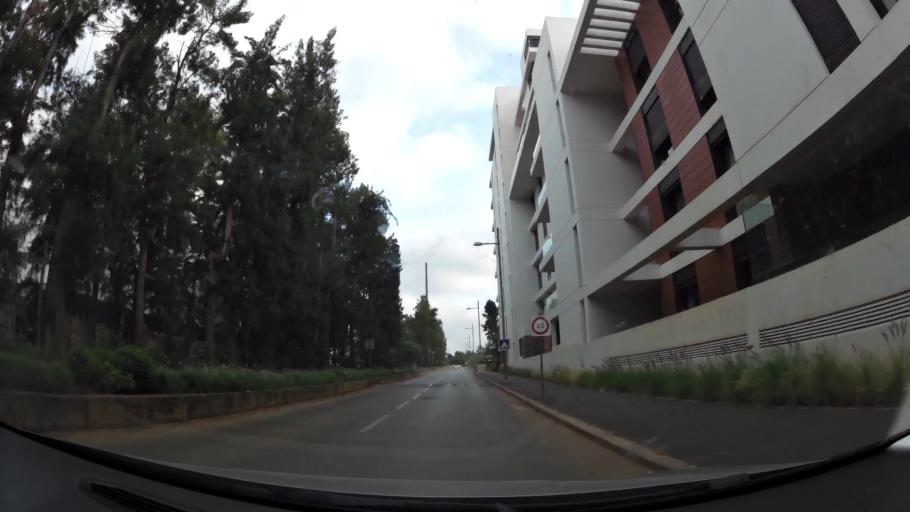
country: MA
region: Rabat-Sale-Zemmour-Zaer
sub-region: Rabat
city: Rabat
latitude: 33.9507
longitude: -6.8332
